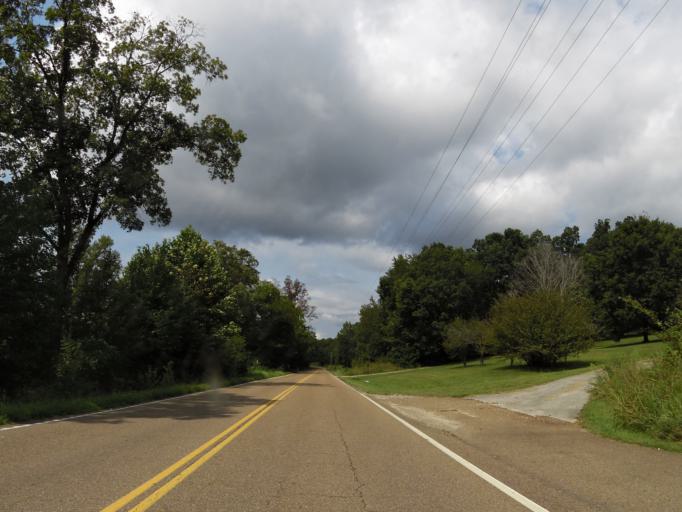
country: US
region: Tennessee
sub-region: Perry County
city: Linden
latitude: 35.6167
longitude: -87.8904
